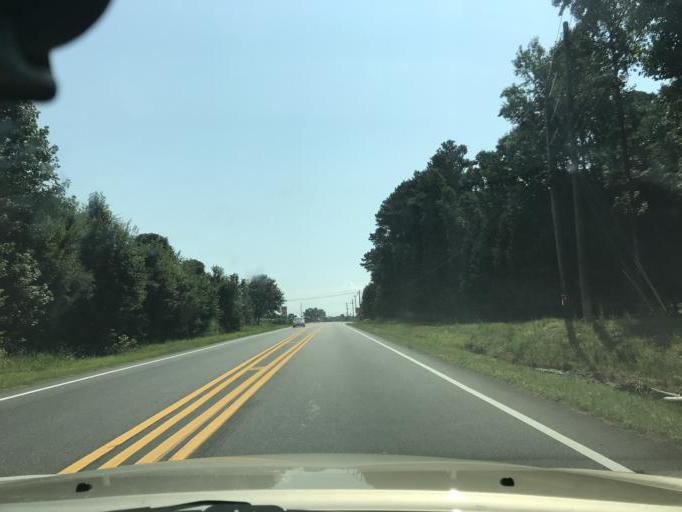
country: US
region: Georgia
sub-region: Hall County
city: Flowery Branch
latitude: 34.2512
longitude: -84.0020
